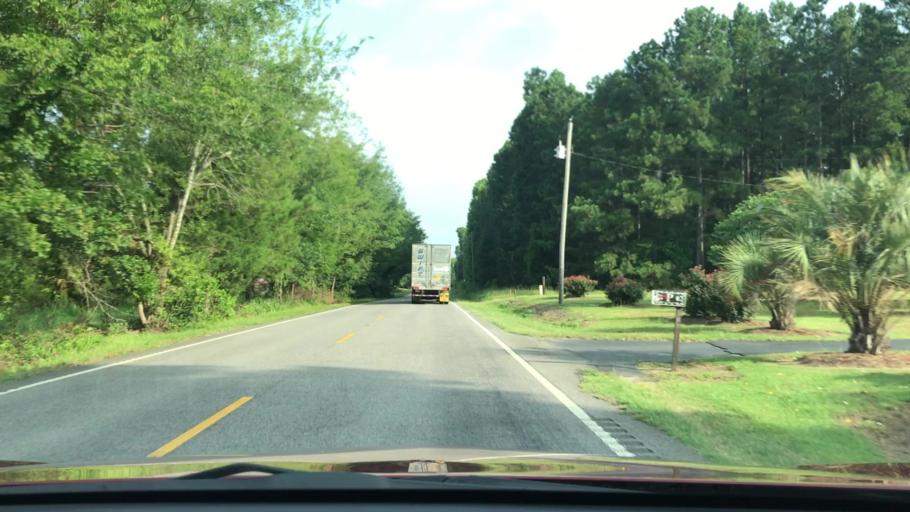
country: US
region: South Carolina
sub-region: Barnwell County
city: Williston
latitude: 33.6167
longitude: -81.2861
